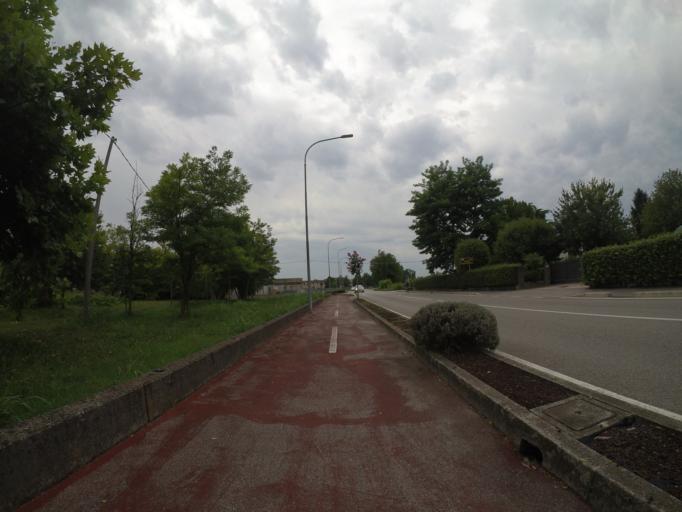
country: IT
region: Friuli Venezia Giulia
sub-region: Provincia di Udine
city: Varmo
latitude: 45.8823
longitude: 12.9906
